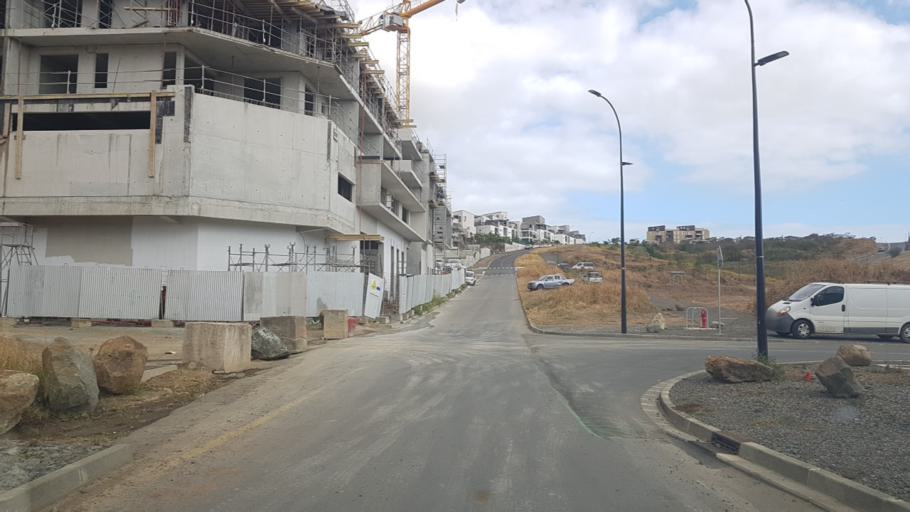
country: NC
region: South Province
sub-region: Dumbea
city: Dumbea
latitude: -22.1971
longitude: 166.4433
